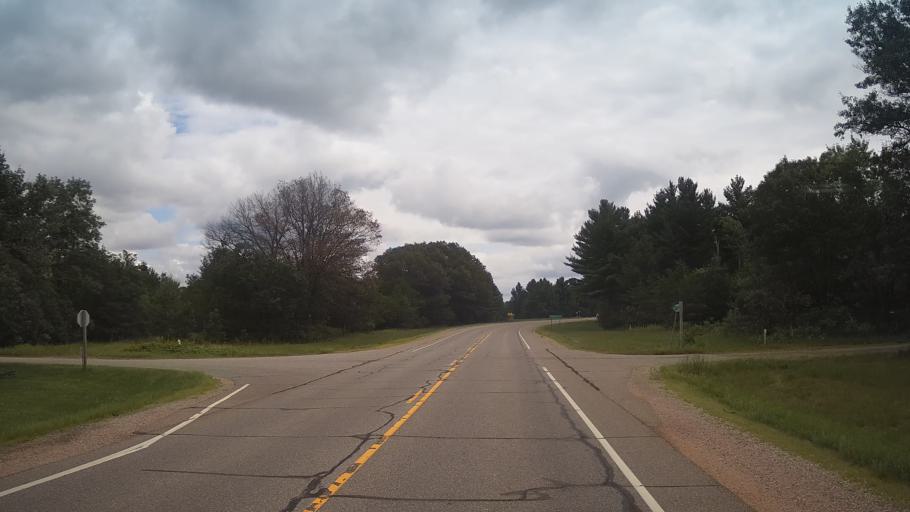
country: US
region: Wisconsin
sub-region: Adams County
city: Friendship
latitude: 44.0467
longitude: -89.9763
